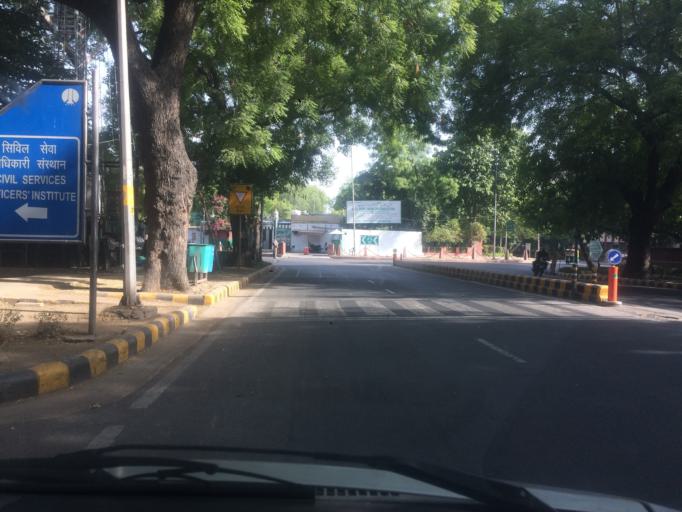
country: IN
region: NCT
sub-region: New Delhi
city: New Delhi
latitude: 28.6190
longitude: 77.2278
